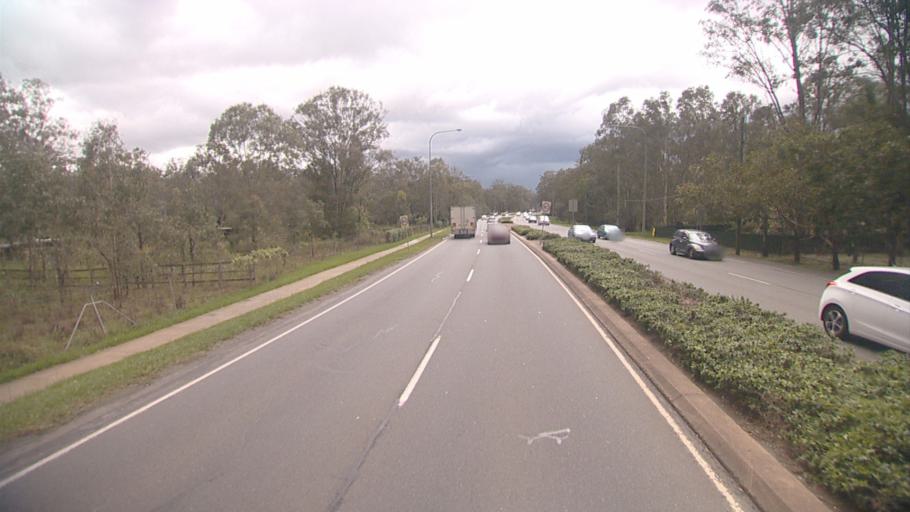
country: AU
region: Queensland
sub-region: Logan
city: Slacks Creek
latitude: -27.6507
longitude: 153.1448
